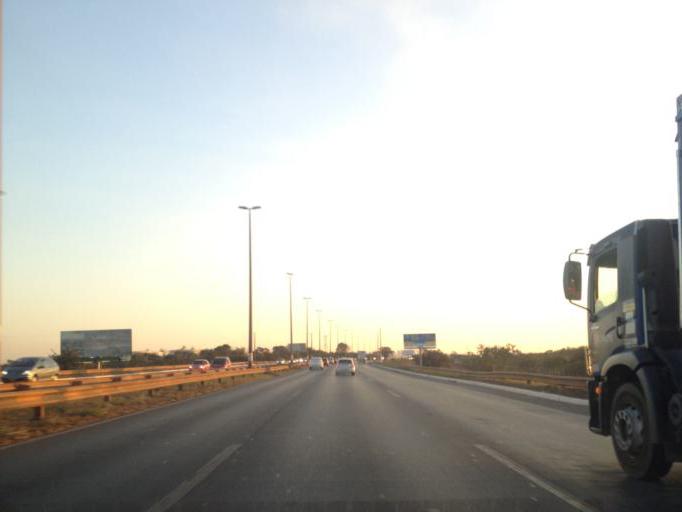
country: BR
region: Federal District
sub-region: Brasilia
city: Brasilia
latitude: -15.7910
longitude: -47.9523
